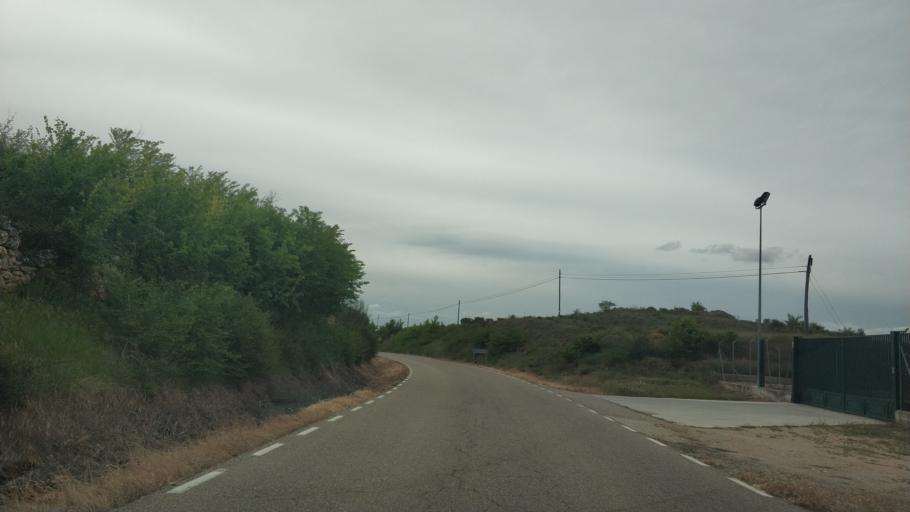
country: ES
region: Castille and Leon
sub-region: Provincia de Soria
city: Berlanga de Duero
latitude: 41.4795
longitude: -2.8623
